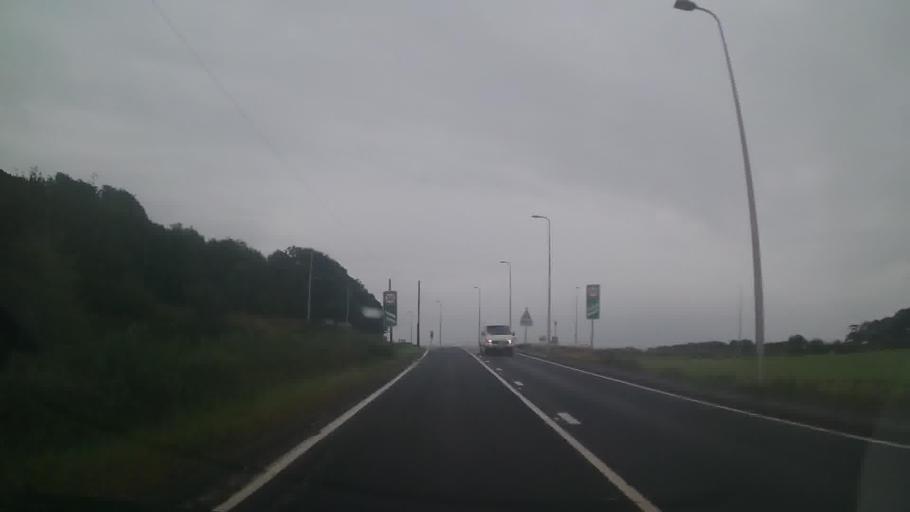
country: GB
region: Scotland
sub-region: North Ayrshire
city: West Kilbride
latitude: 55.6959
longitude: -4.8685
